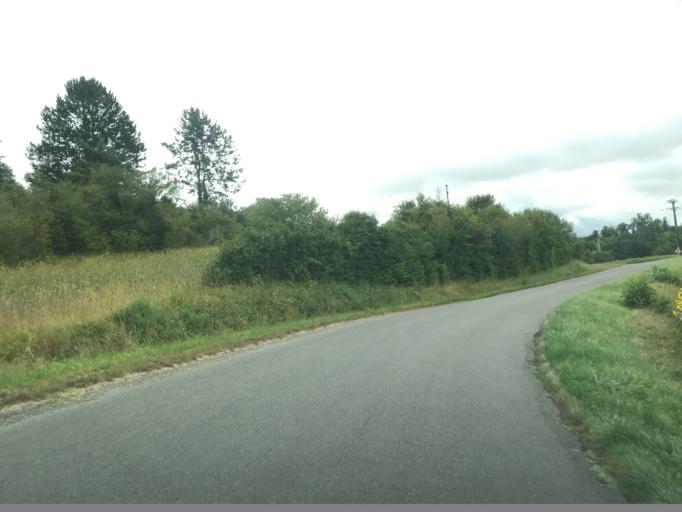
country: FR
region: Poitou-Charentes
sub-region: Departement de la Charente
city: Dirac
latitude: 45.5675
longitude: 0.2117
